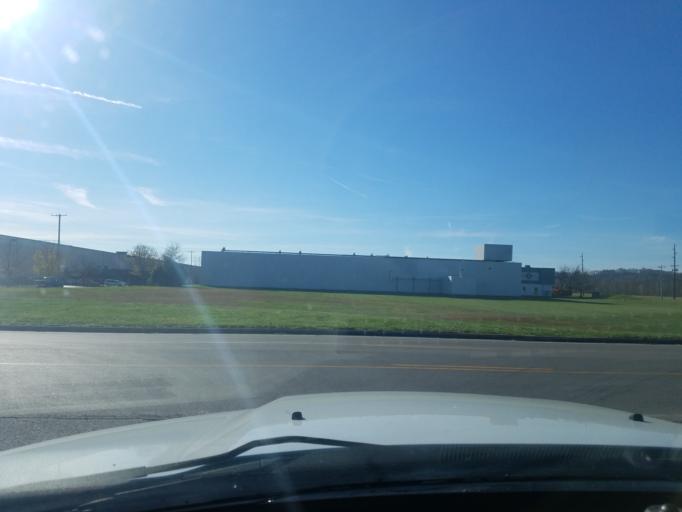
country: US
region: Kentucky
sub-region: Jefferson County
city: Pleasure Ridge Park
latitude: 38.1399
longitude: -85.8961
